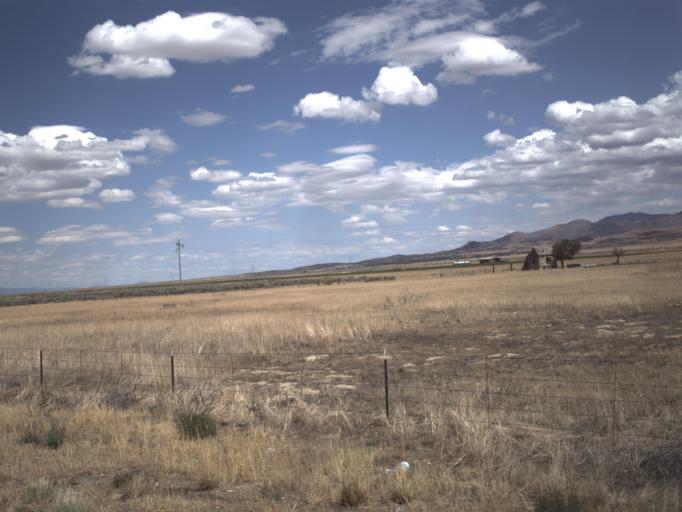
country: US
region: Utah
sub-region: Millard County
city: Delta
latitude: 39.2180
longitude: -112.4190
